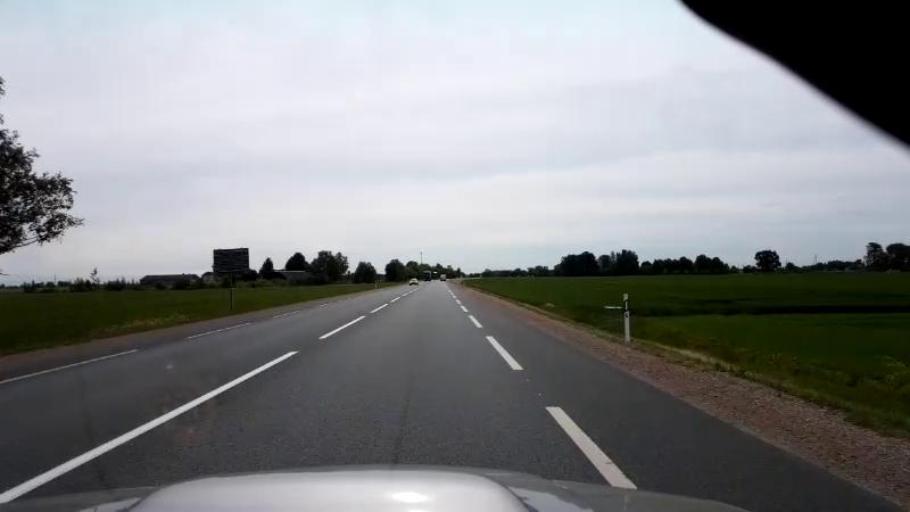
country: LV
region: Bauskas Rajons
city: Bauska
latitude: 56.4354
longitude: 24.1765
